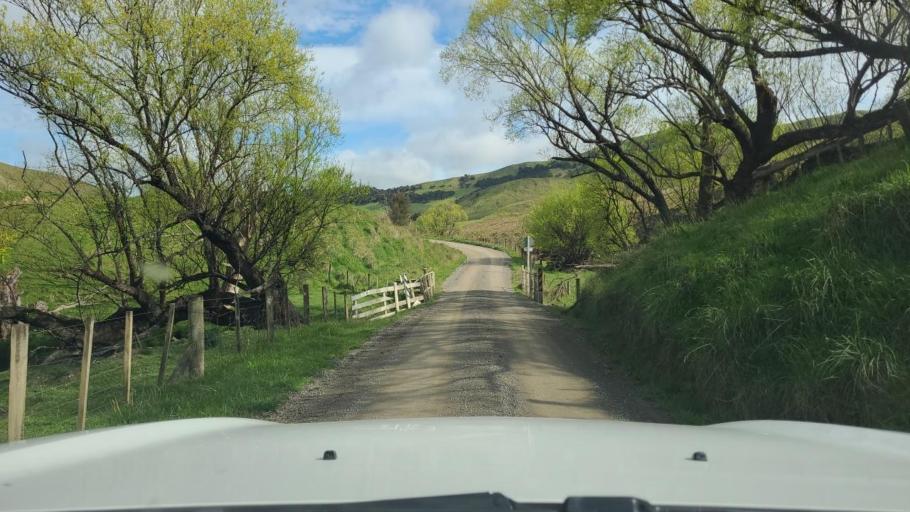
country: NZ
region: Wellington
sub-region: South Wairarapa District
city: Waipawa
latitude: -41.2944
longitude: 175.6484
